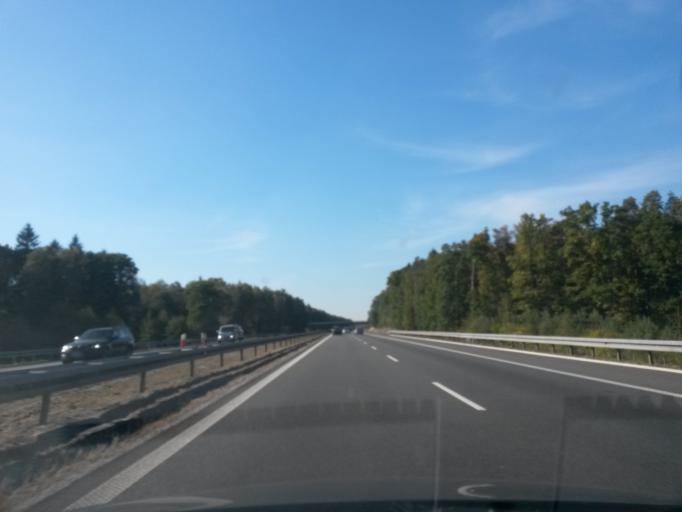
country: PL
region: Opole Voivodeship
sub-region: Powiat opolski
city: Proszkow
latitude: 50.5820
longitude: 17.8301
